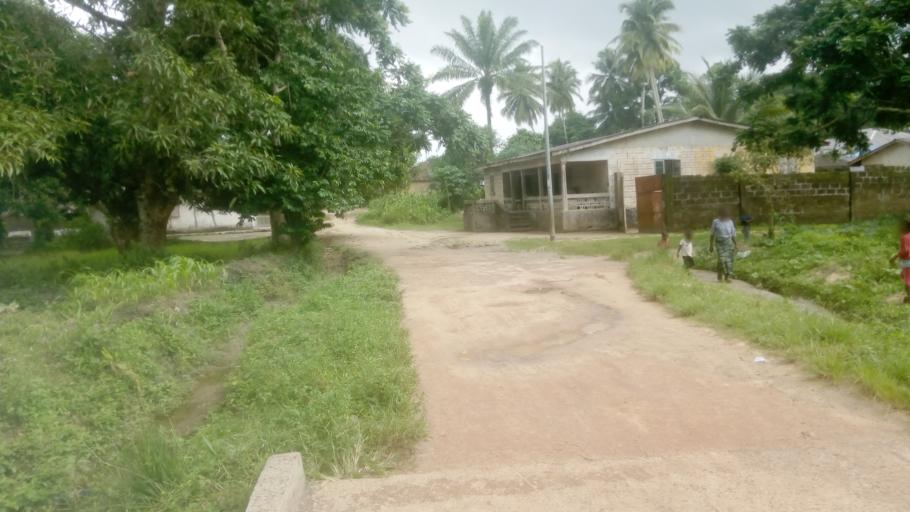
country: SL
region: Northern Province
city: Lunsar
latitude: 8.6848
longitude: -12.5409
